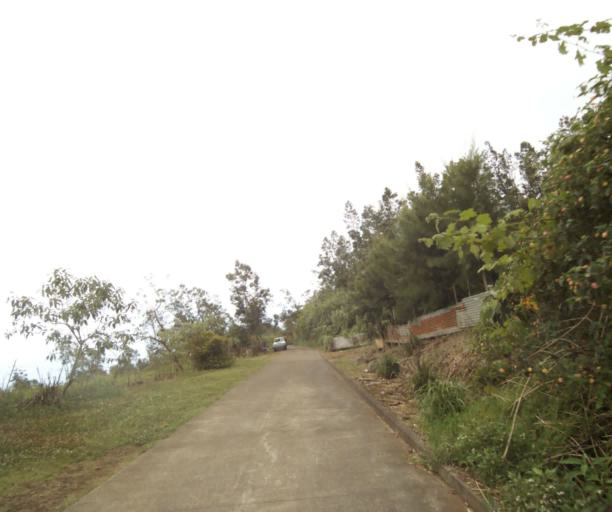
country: RE
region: Reunion
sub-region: Reunion
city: Saint-Paul
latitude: -21.0148
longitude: 55.3537
